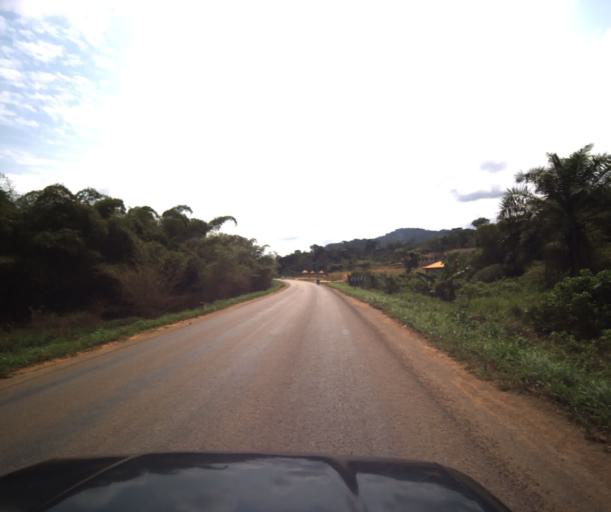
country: CM
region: Centre
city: Eseka
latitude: 3.8558
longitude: 10.5362
